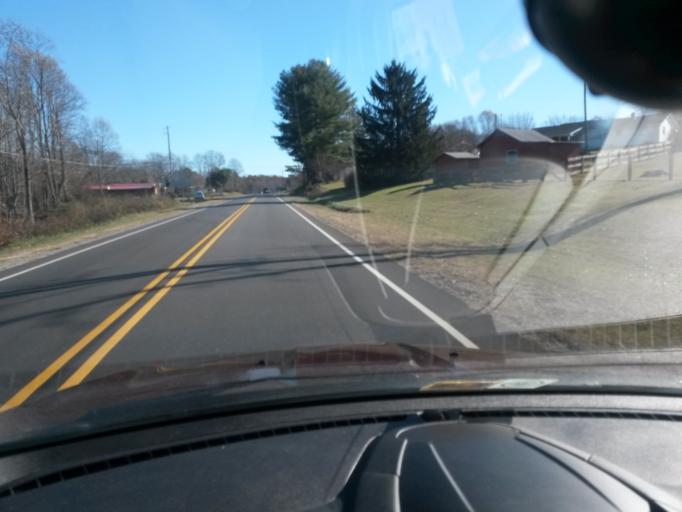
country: US
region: Virginia
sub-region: Henry County
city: Pannill Fork
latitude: 36.7508
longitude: -80.0743
